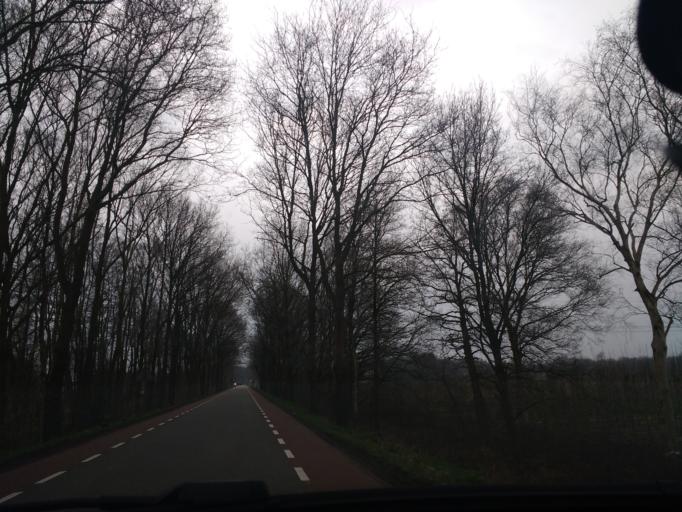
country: NL
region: Utrecht
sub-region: Gemeente Utrechtse Heuvelrug
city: Overberg
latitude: 52.0344
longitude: 5.5244
